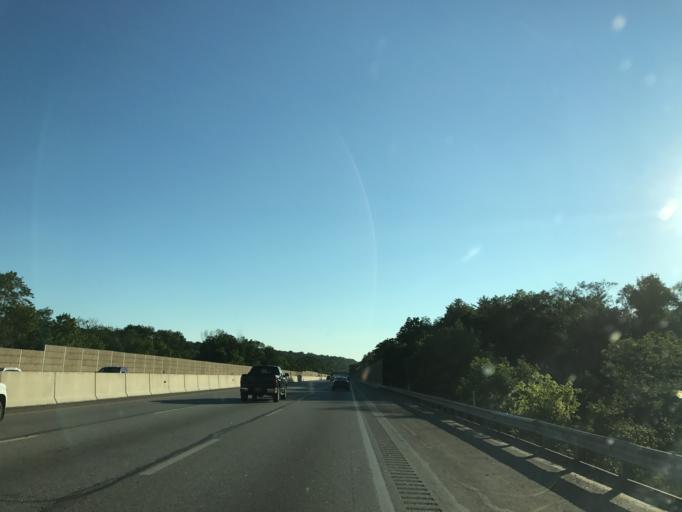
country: US
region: Pennsylvania
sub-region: Montgomery County
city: Fort Washington
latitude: 40.1275
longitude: -75.2194
